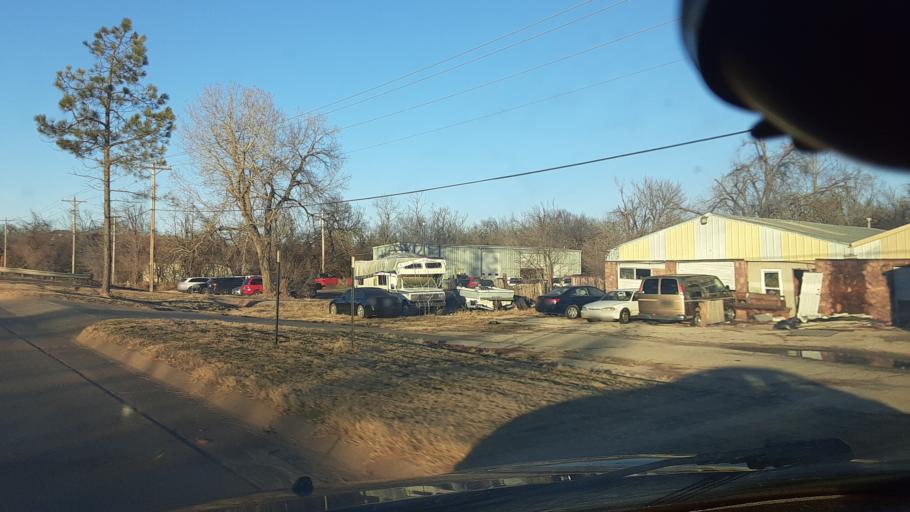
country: US
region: Oklahoma
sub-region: Logan County
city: Guthrie
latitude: 35.8366
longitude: -97.4254
